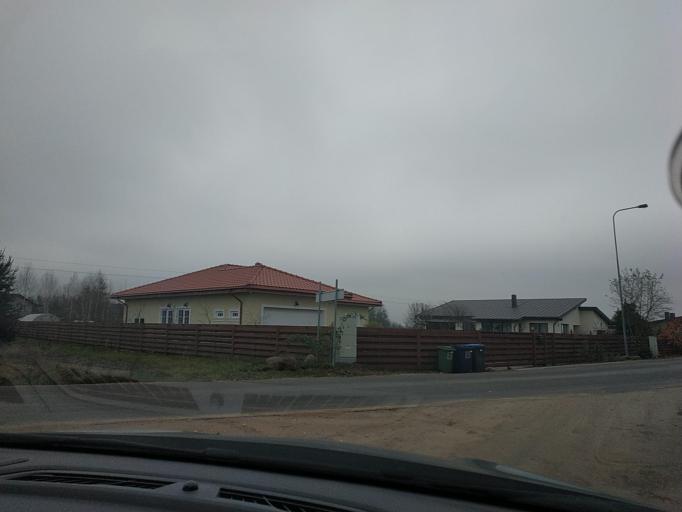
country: LT
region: Vilnius County
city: Rasos
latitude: 54.6378
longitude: 25.3323
